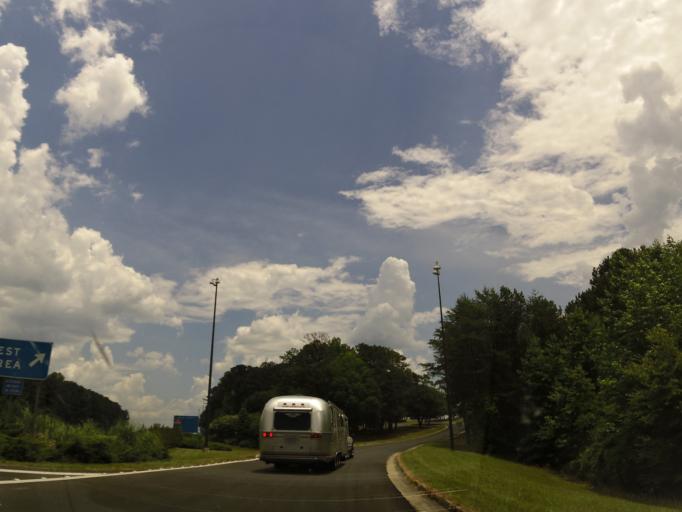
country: US
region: Alabama
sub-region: Sumter County
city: York
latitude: 32.4495
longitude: -88.4001
